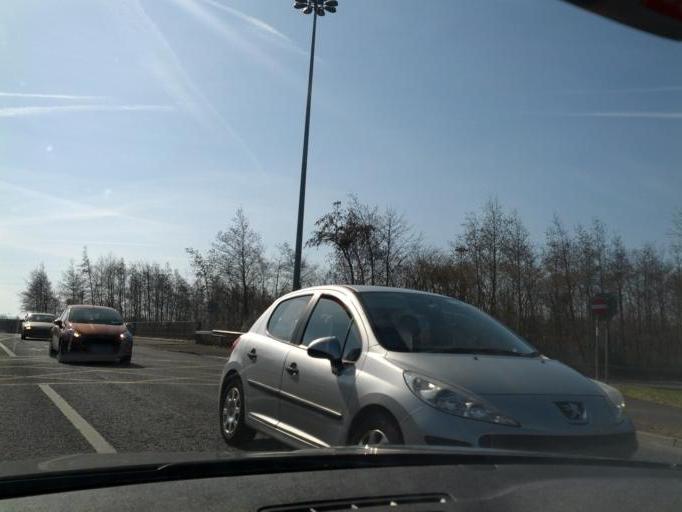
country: IE
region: Leinster
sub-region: Kildare
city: Leixlip
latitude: 53.3592
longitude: -6.4746
